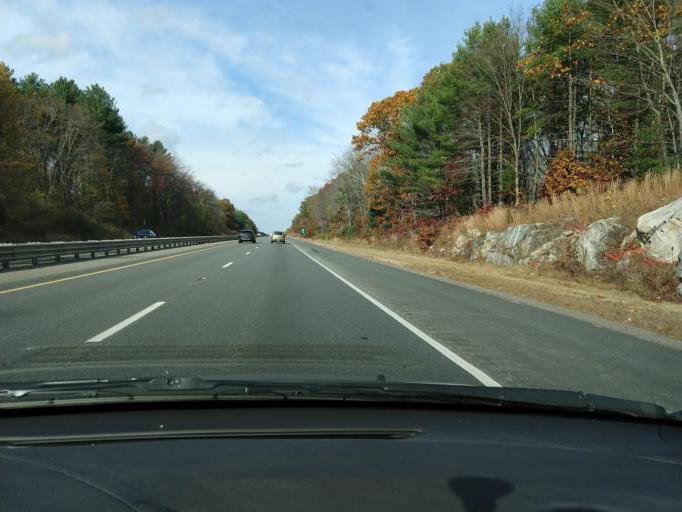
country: US
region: Massachusetts
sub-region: Middlesex County
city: Acton
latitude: 42.4954
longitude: -71.4659
